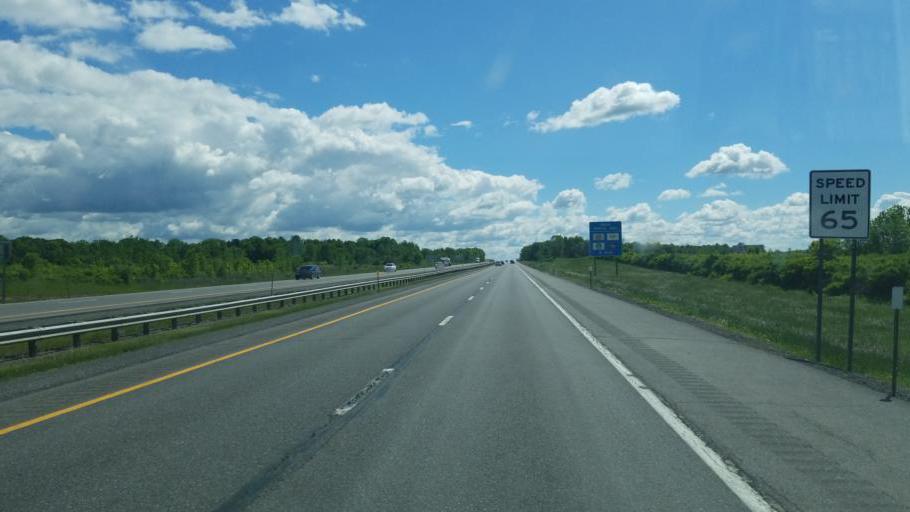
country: US
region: New York
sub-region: Oneida County
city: Vernon
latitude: 43.1251
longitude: -75.5703
